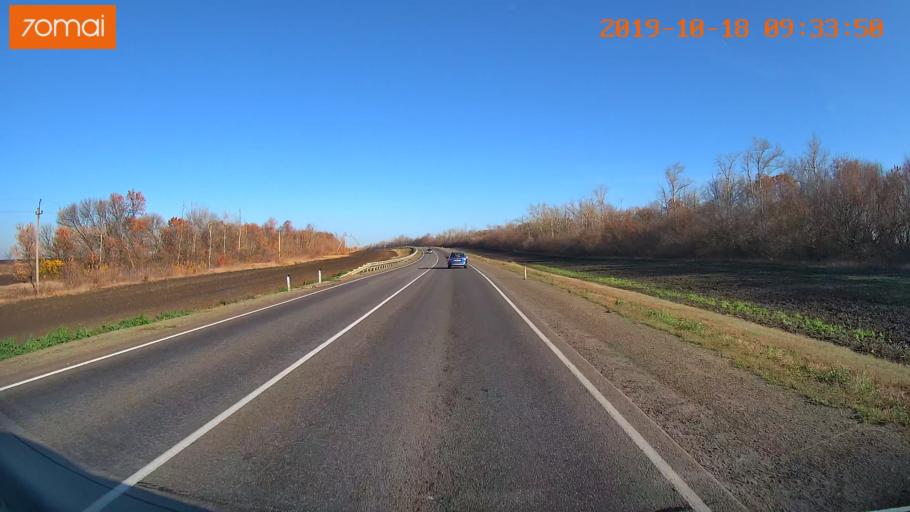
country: RU
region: Tula
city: Yefremov
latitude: 53.1722
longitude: 38.1523
